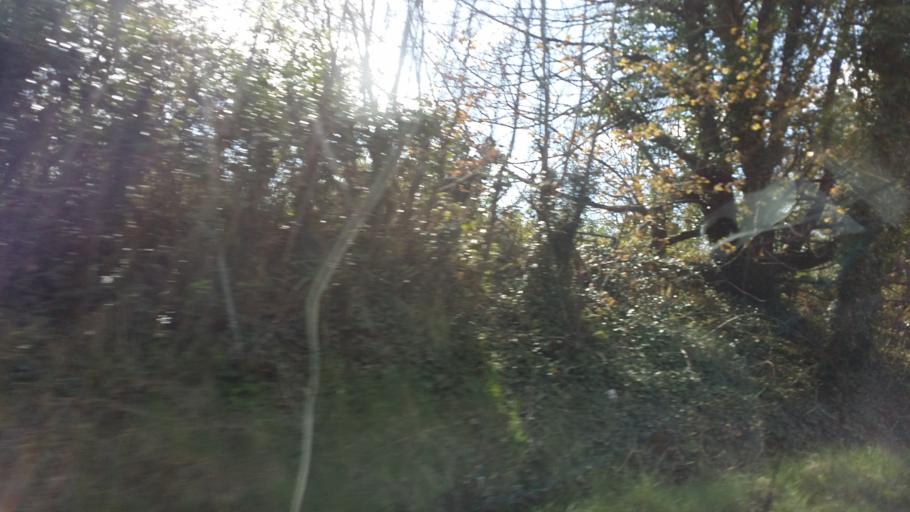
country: IE
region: Ulster
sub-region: County Donegal
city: Ballyshannon
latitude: 54.4936
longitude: -8.1666
